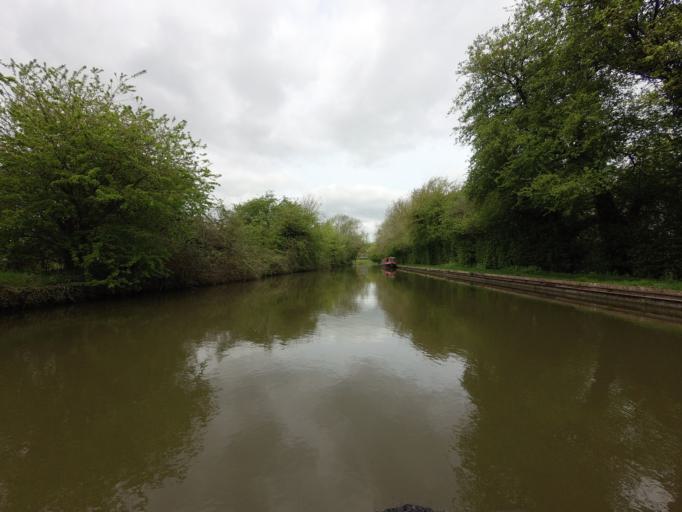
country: GB
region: England
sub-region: Milton Keynes
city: Simpson
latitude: 52.0147
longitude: -0.7194
